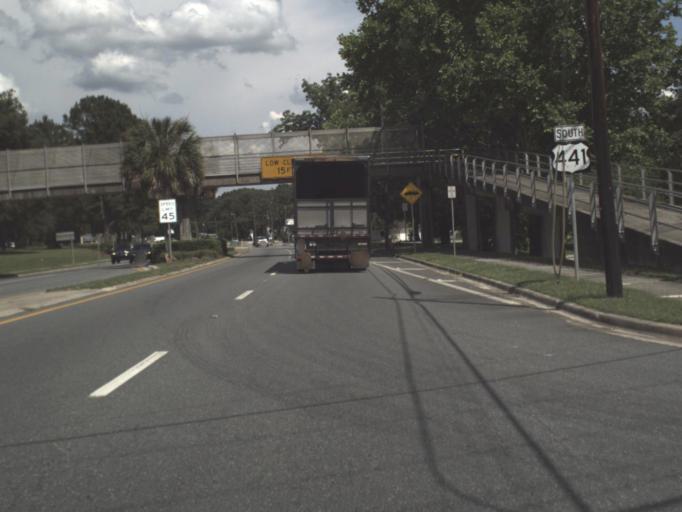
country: US
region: Florida
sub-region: Alachua County
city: Alachua
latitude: 29.7936
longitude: -82.4942
